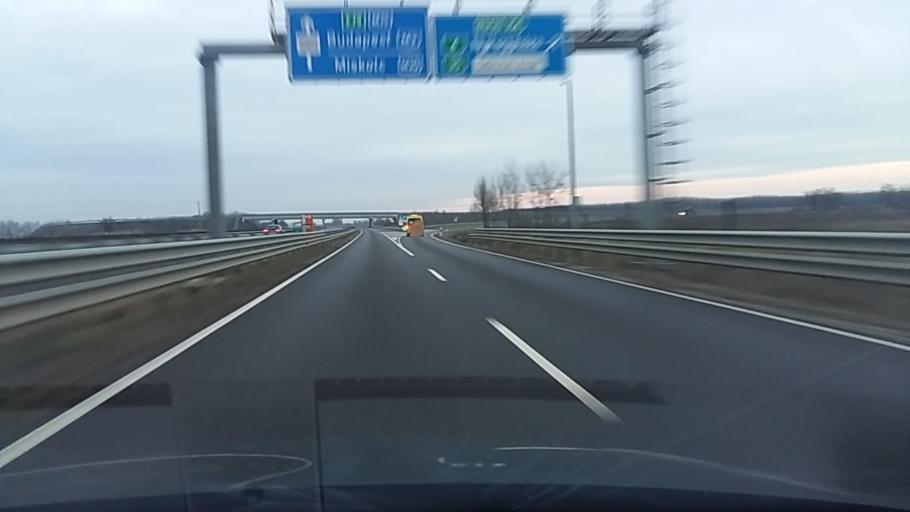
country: HU
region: Hajdu-Bihar
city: Debrecen
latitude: 47.5585
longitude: 21.5500
